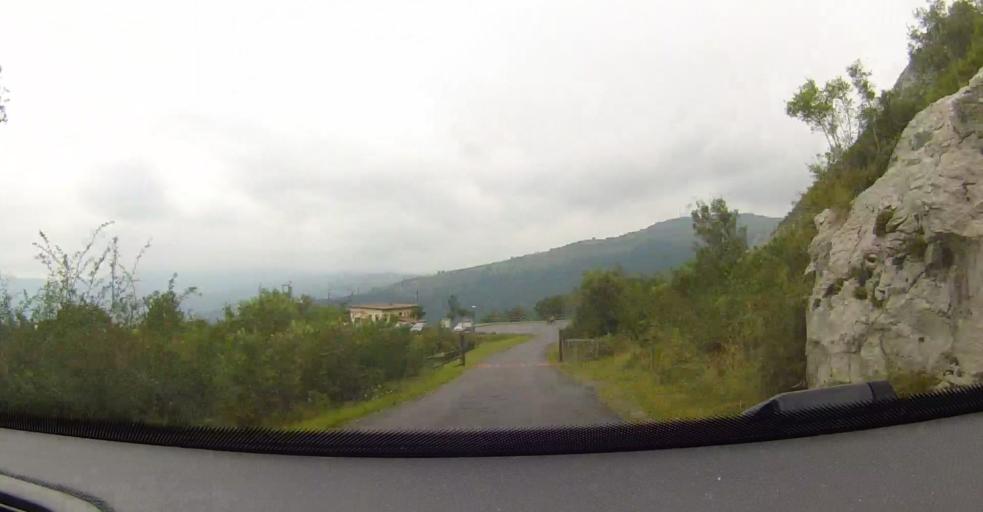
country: ES
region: Cantabria
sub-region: Provincia de Cantabria
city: Rasines
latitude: 43.2604
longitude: -3.3839
